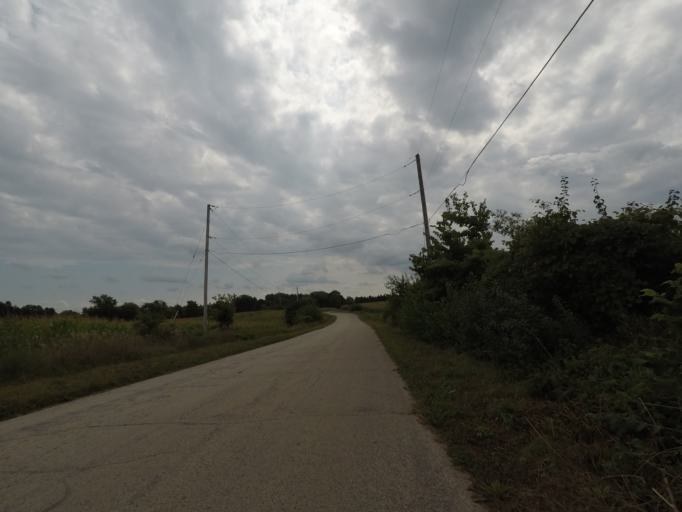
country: US
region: Wisconsin
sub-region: Jefferson County
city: Lake Koshkonong
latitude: 42.8948
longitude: -88.8735
